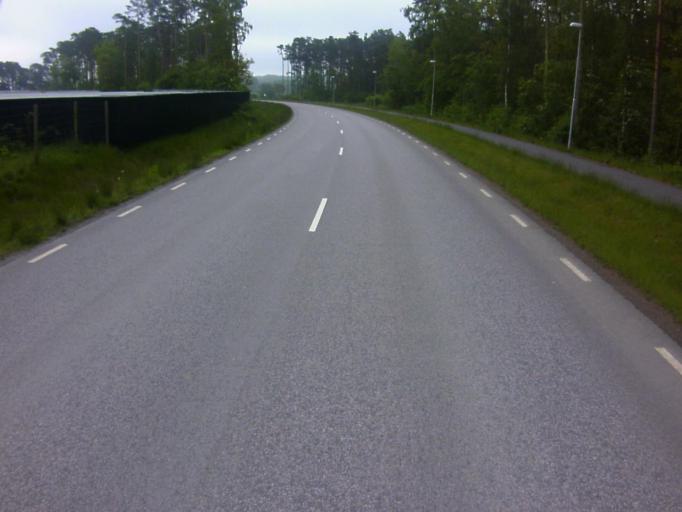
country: SE
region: Blekinge
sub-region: Solvesborgs Kommun
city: Soelvesborg
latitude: 56.0449
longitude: 14.6109
